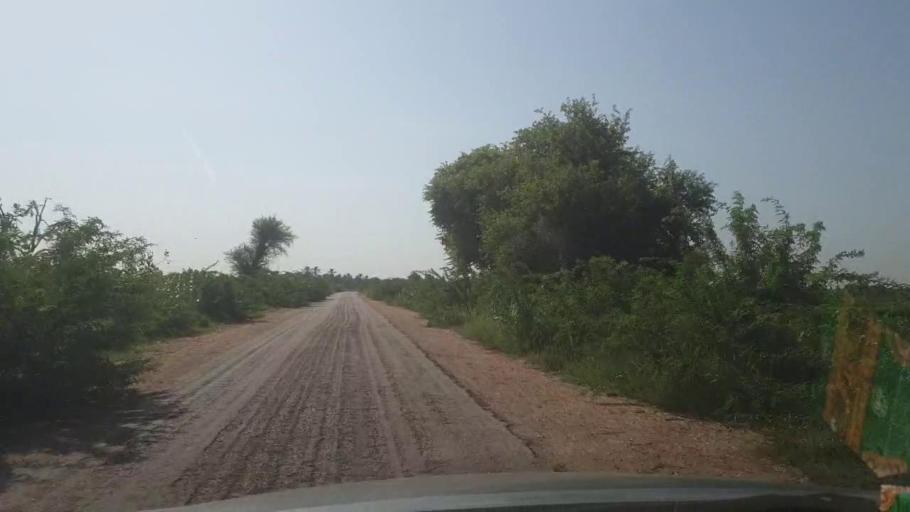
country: PK
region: Sindh
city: Rohri
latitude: 27.4711
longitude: 69.0341
